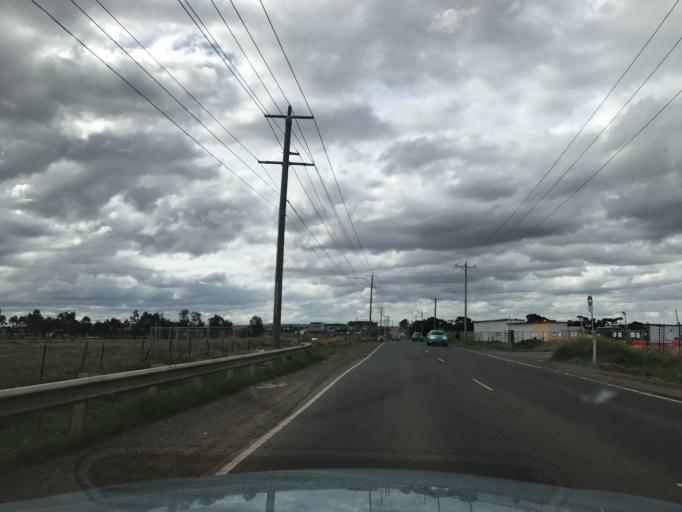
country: AU
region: Victoria
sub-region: Wyndham
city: Williams Landing
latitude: -37.8507
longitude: 144.7455
